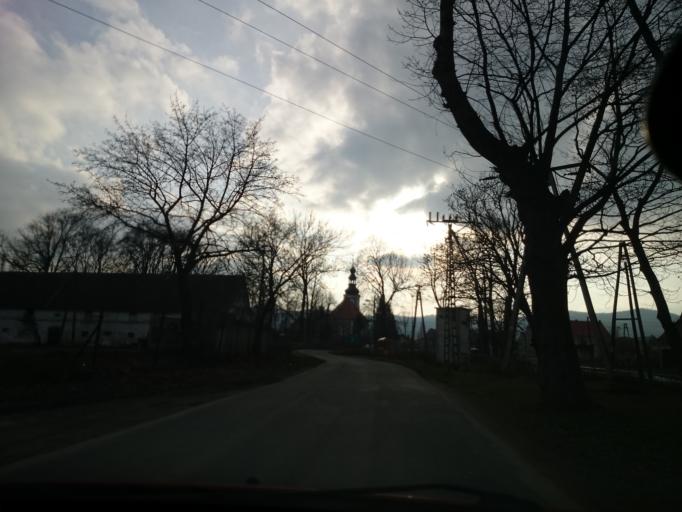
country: PL
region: Lower Silesian Voivodeship
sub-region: Powiat zabkowicki
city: Bardo
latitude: 50.5399
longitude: 16.7339
